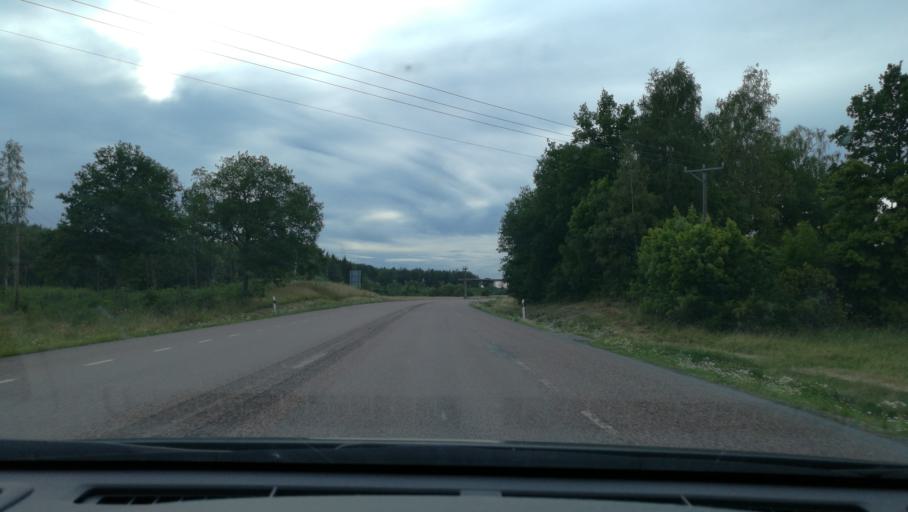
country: SE
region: Vaestmanland
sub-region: Kungsors Kommun
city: Kungsoer
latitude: 59.4519
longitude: 16.0325
